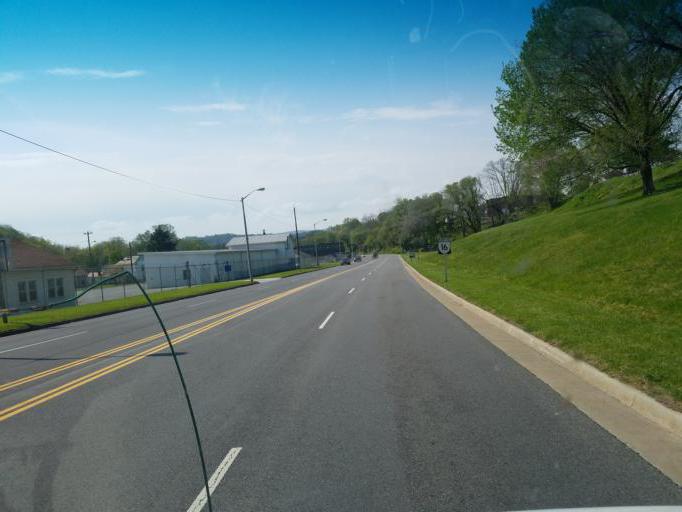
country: US
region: Virginia
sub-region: Smyth County
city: Marion
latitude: 36.8284
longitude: -81.5095
